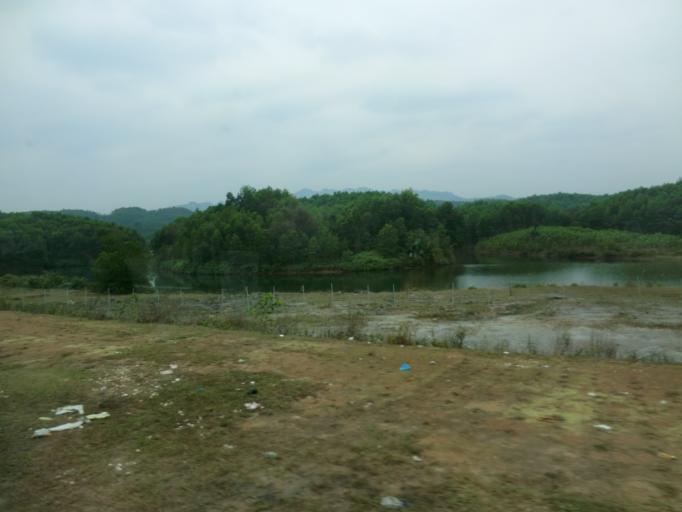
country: VN
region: Yen Bai
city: Co Phuc
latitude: 21.7321
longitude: 104.8251
